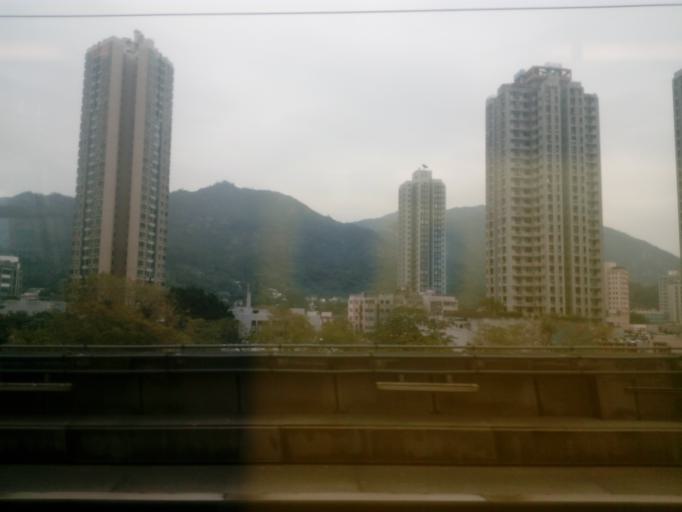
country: HK
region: Tuen Mun
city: Tuen Mun
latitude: 22.3997
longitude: 113.9747
